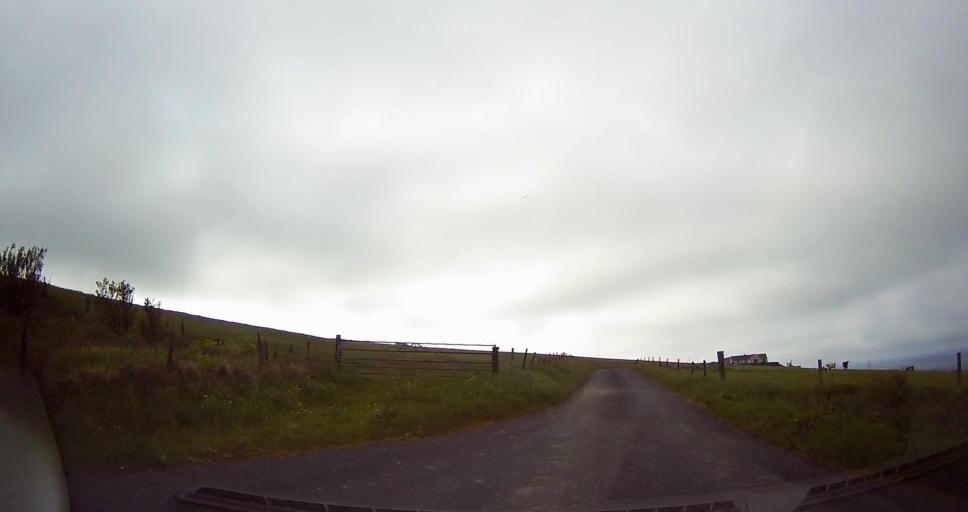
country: GB
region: Scotland
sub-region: Orkney Islands
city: Orkney
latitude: 59.1178
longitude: -3.1309
